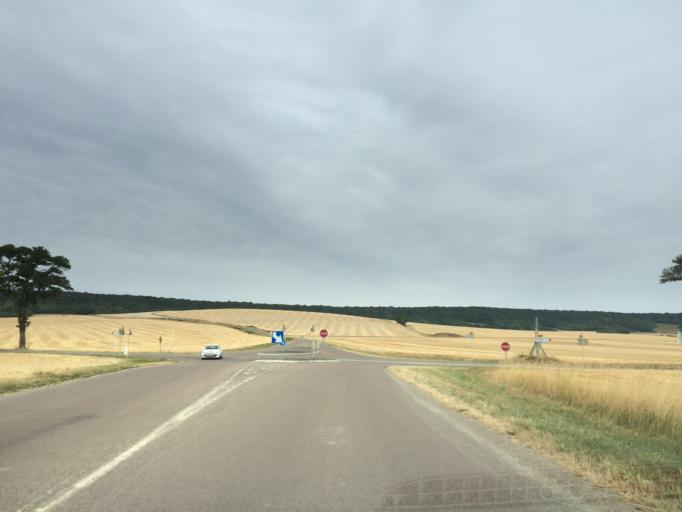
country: FR
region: Bourgogne
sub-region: Departement de l'Yonne
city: Aillant-sur-Tholon
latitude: 47.8515
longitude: 3.3281
